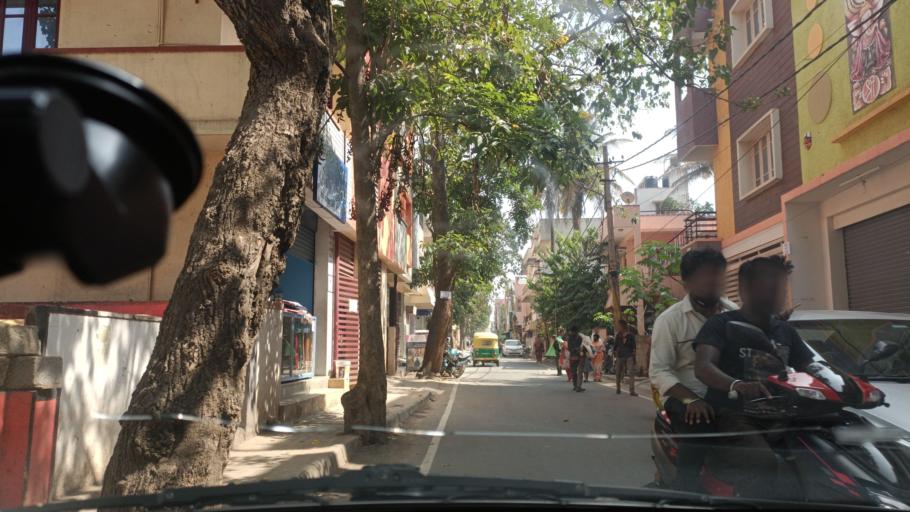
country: IN
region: Karnataka
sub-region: Bangalore Urban
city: Yelahanka
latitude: 13.1111
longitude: 77.6057
